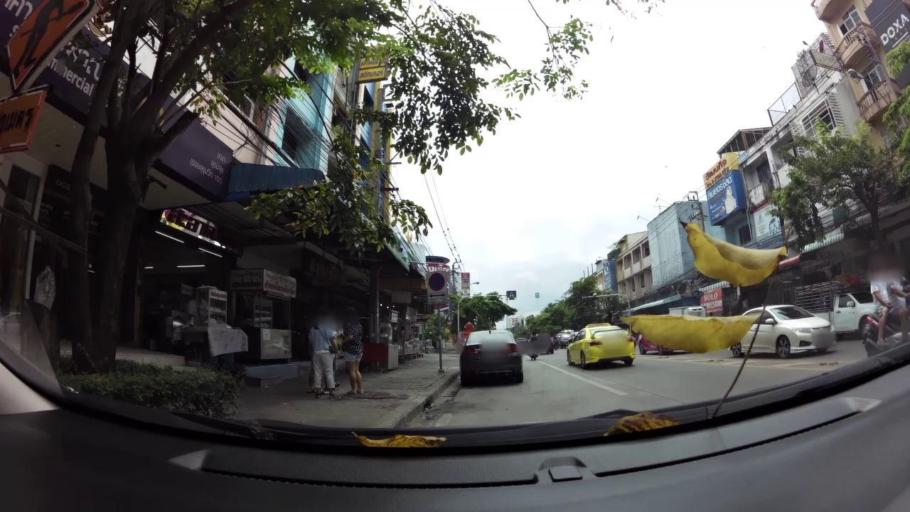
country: TH
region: Bangkok
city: Bang Na
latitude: 13.6780
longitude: 100.6332
